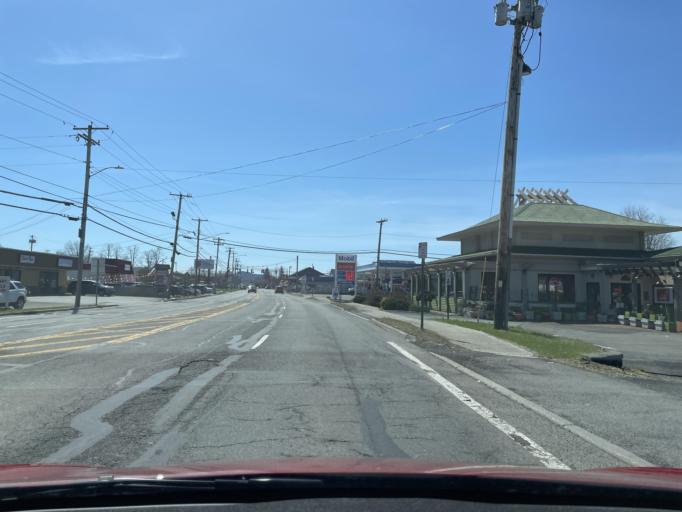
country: US
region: New York
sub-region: Ulster County
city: Lincoln Park
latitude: 41.9562
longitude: -73.9944
